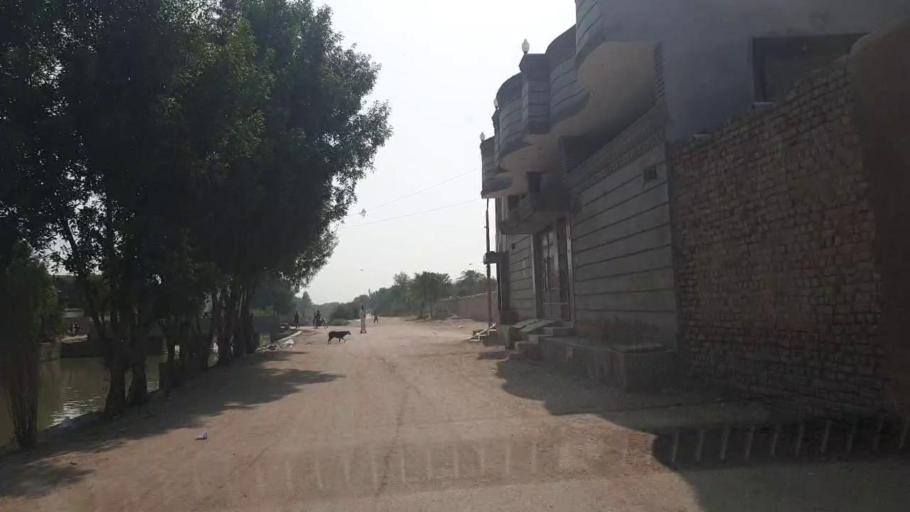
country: PK
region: Sindh
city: Badin
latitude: 24.6549
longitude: 68.8421
